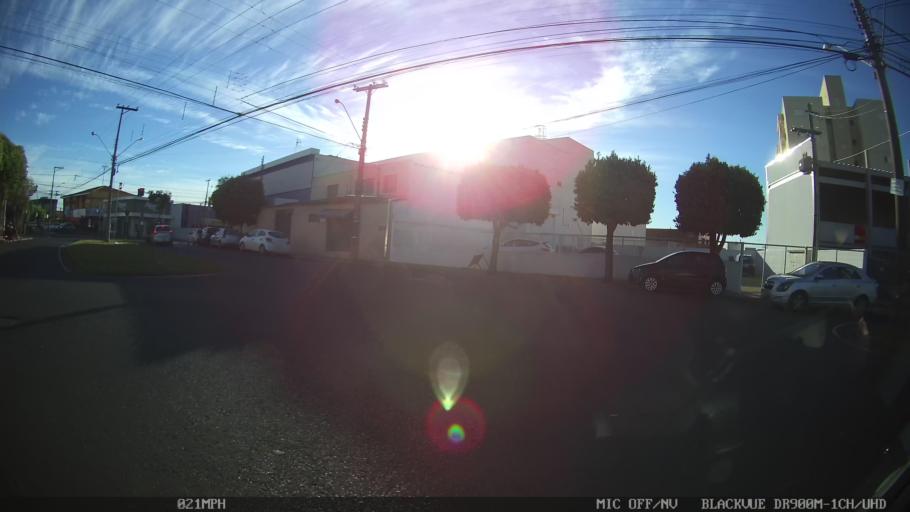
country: BR
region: Sao Paulo
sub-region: Sao Jose Do Rio Preto
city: Sao Jose do Rio Preto
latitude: -20.8281
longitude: -49.3723
